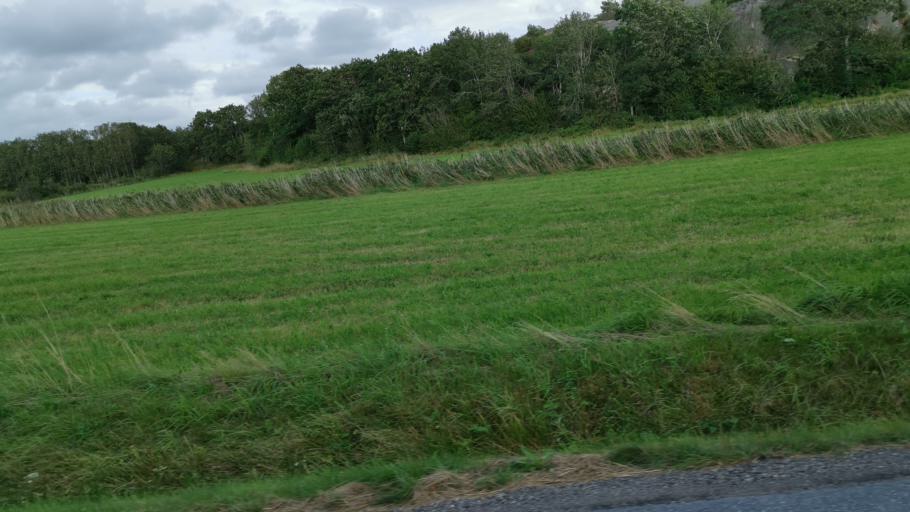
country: SE
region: Vaestra Goetaland
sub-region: Sotenas Kommun
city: Hunnebostrand
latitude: 58.5242
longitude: 11.2973
